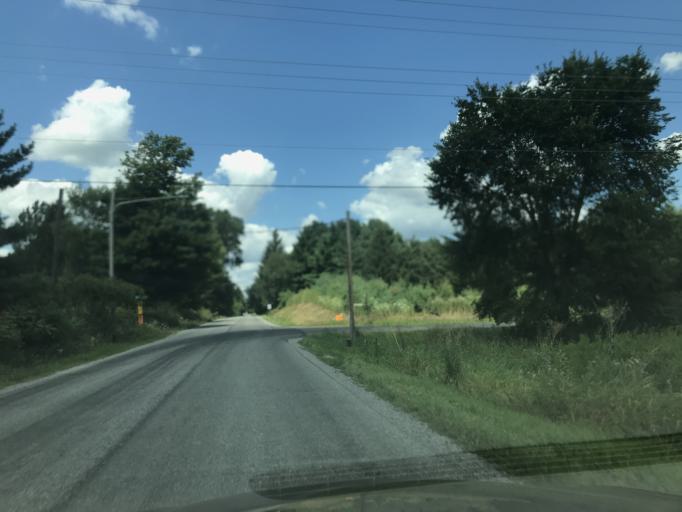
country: US
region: Michigan
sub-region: Ingham County
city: Holt
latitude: 42.6146
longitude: -84.5626
